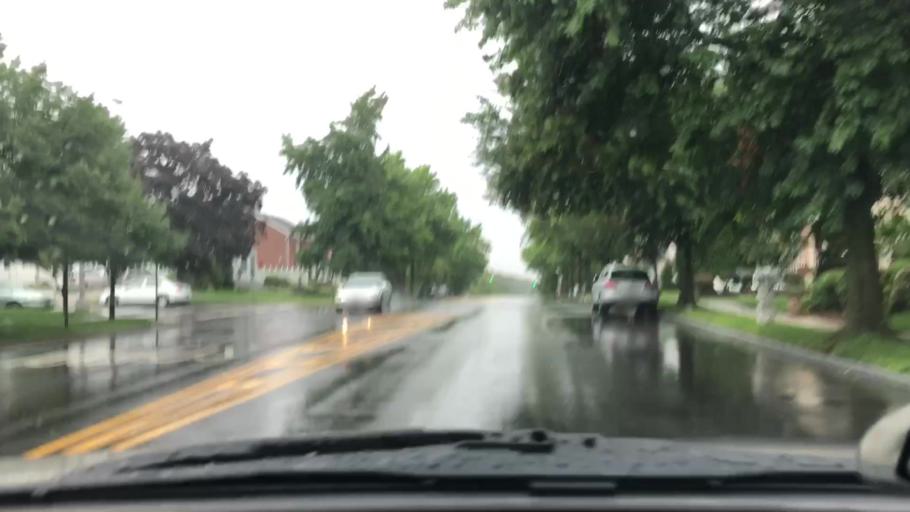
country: US
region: New Jersey
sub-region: Middlesex County
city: Carteret
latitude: 40.5455
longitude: -74.1985
